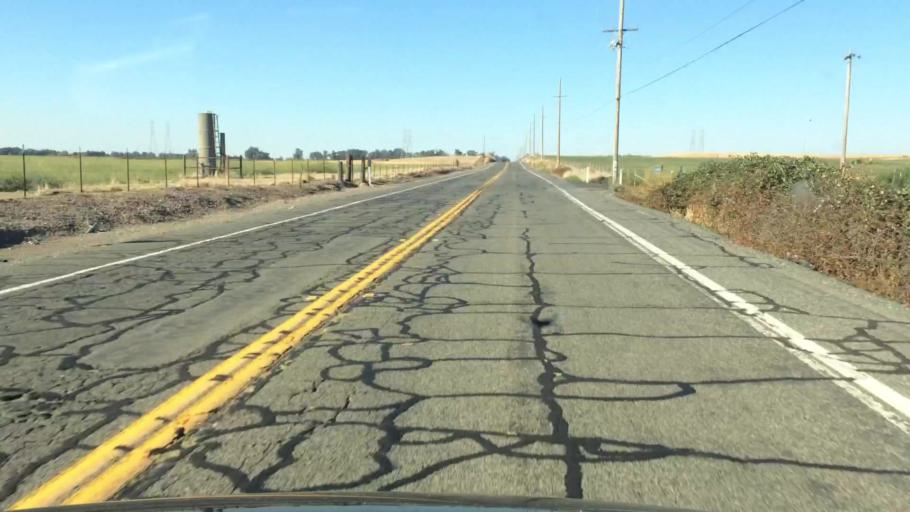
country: US
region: California
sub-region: Sacramento County
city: Clay
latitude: 38.3391
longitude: -121.1684
